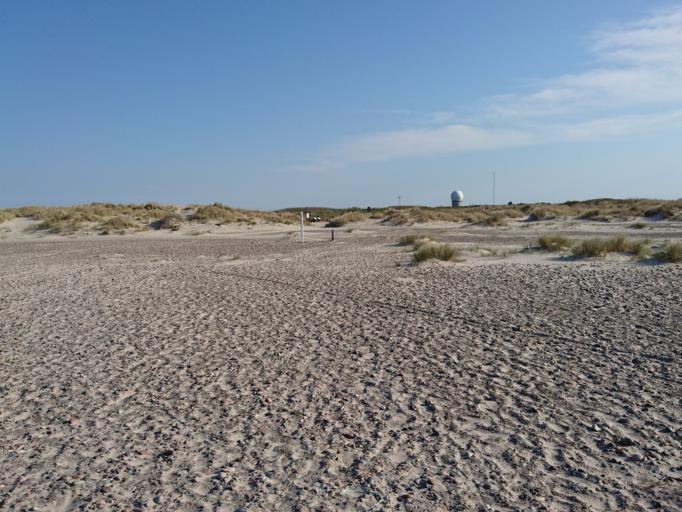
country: DK
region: North Denmark
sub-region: Frederikshavn Kommune
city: Skagen
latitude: 57.7514
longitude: 10.6042
